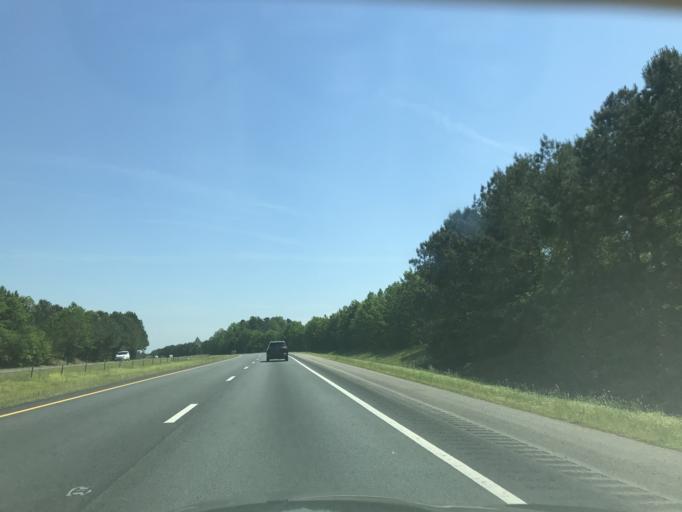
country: US
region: North Carolina
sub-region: Johnston County
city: Benson
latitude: 35.3738
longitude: -78.5024
